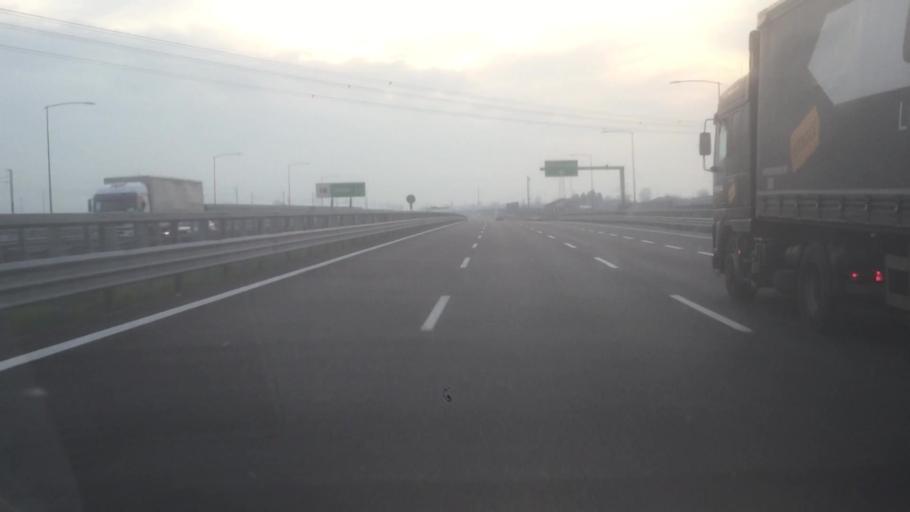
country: IT
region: Lombardy
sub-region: Provincia di Brescia
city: Chiari
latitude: 45.5168
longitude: 9.9242
